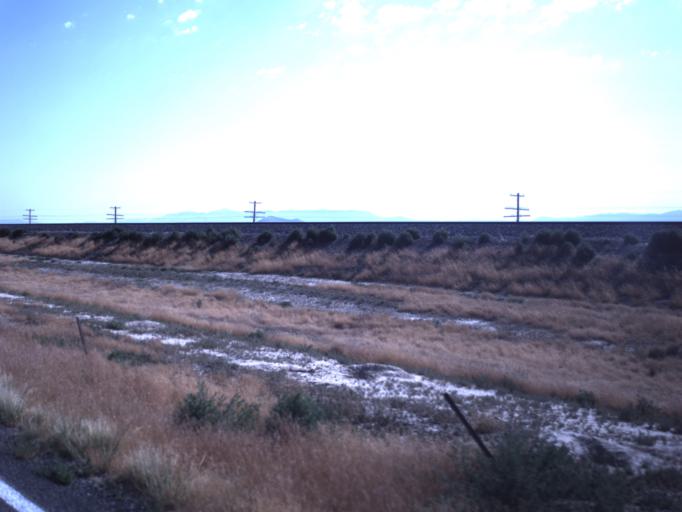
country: US
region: Utah
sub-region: Millard County
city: Delta
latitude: 38.9719
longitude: -112.7987
